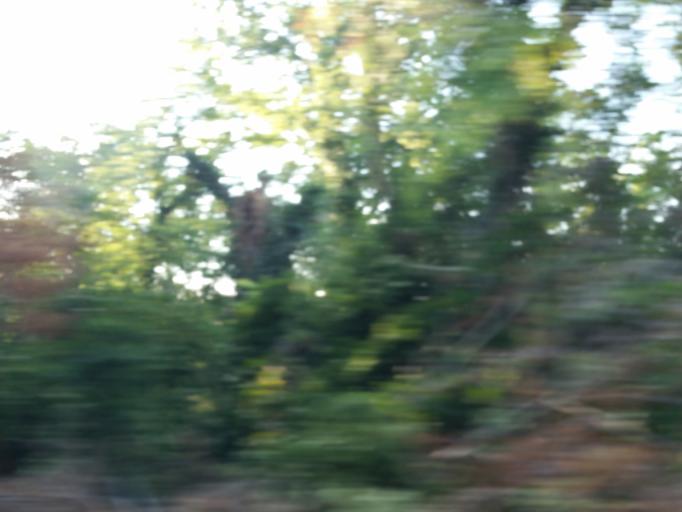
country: US
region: Tennessee
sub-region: Knox County
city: Knoxville
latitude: 35.9280
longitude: -83.9166
